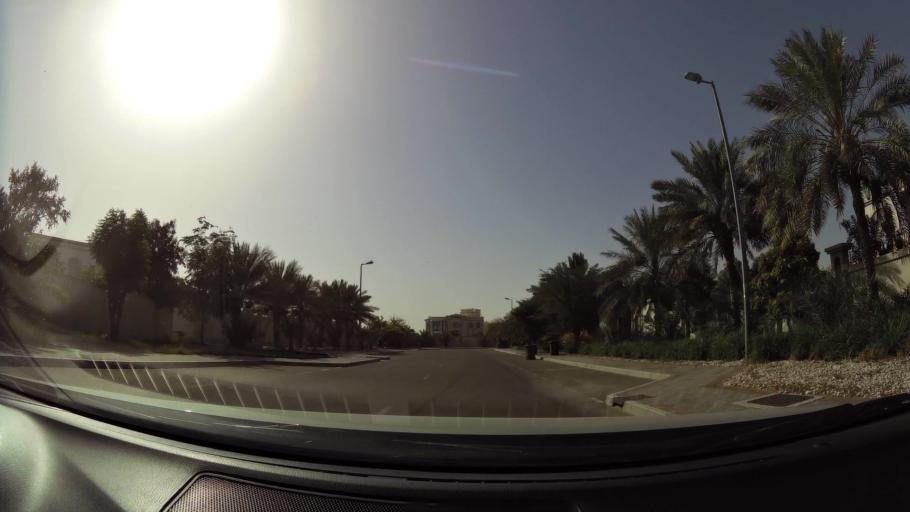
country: OM
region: Al Buraimi
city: Al Buraymi
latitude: 24.3492
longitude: 55.7958
